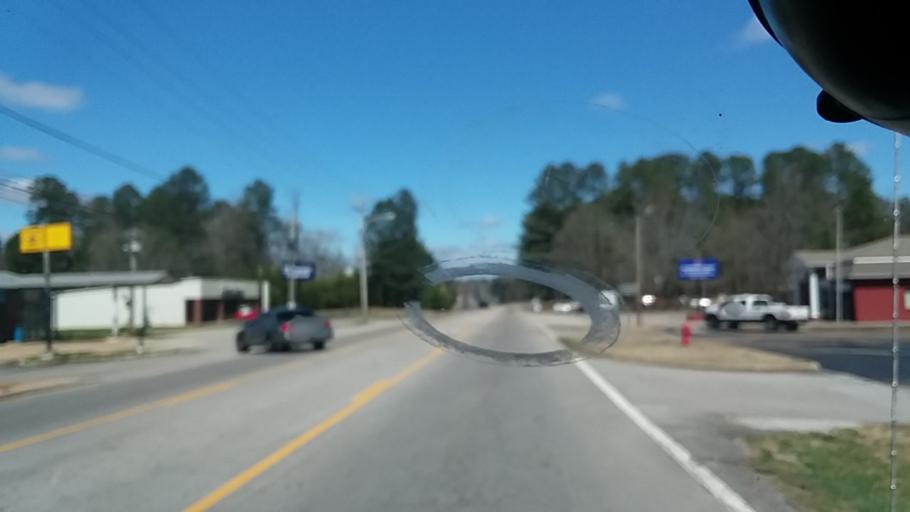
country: US
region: Mississippi
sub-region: Tishomingo County
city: Iuka
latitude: 34.8049
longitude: -88.2022
